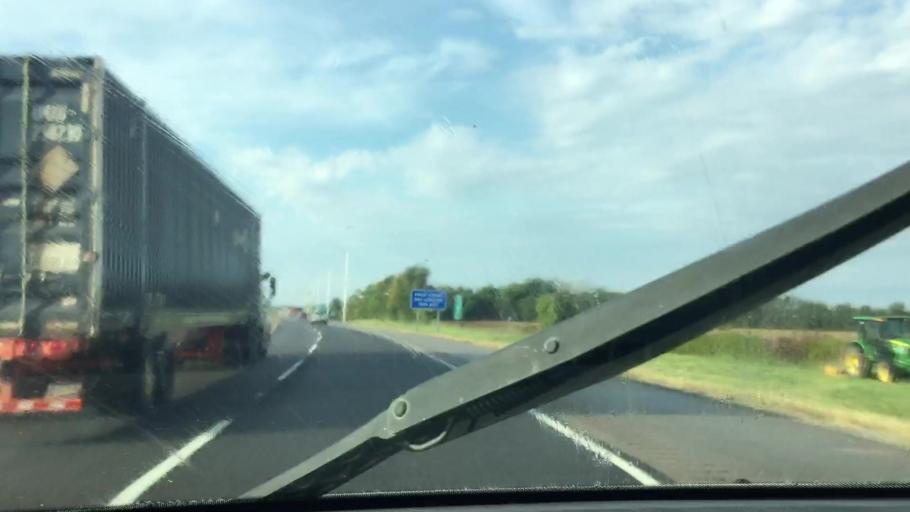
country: US
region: Illinois
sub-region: Whiteside County
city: Rock Falls
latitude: 41.7645
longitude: -89.6296
